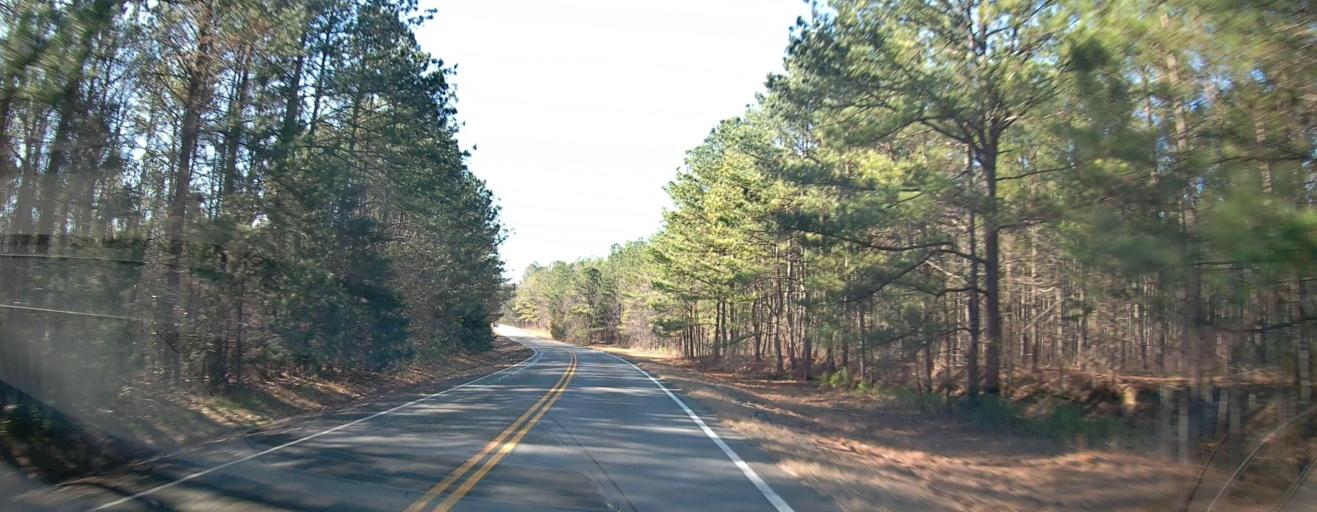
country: US
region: Georgia
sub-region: Talbot County
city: Talbotton
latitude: 32.6499
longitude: -84.4443
